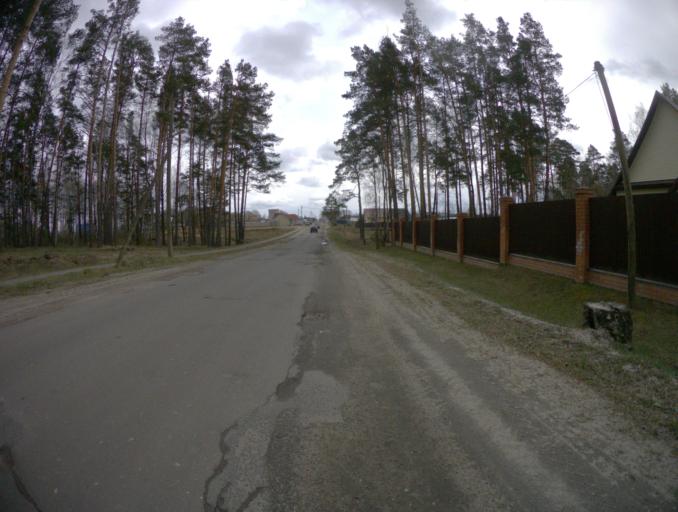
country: RU
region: Vladimir
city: Sudogda
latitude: 56.0706
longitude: 40.7925
